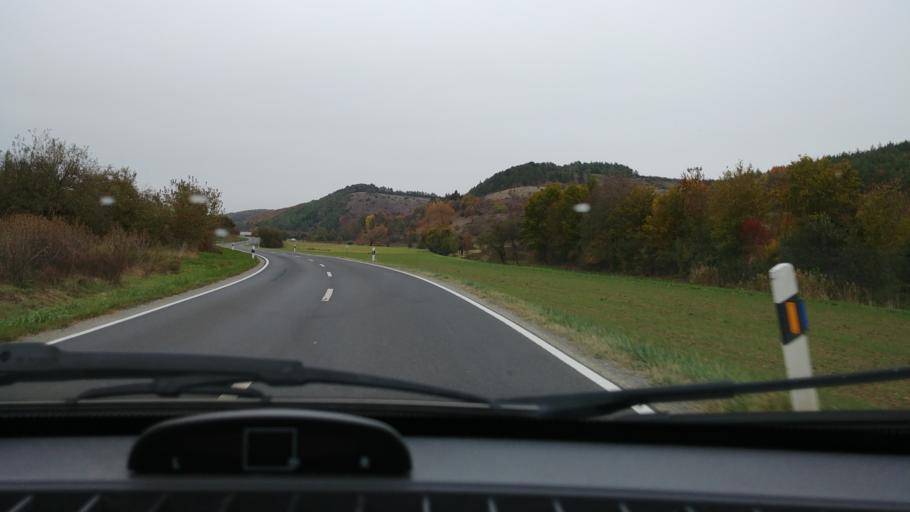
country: DE
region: Baden-Wuerttemberg
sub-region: Regierungsbezirk Stuttgart
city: Werbach
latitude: 49.6941
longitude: 9.6521
